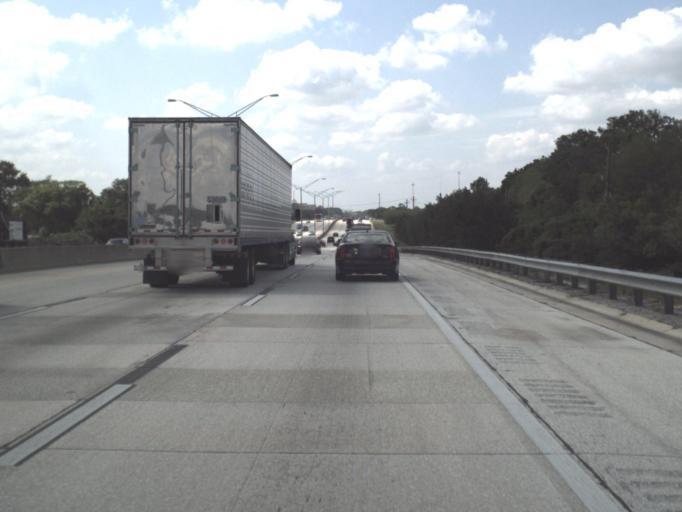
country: US
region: Florida
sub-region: Duval County
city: Jacksonville
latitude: 30.2651
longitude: -81.6089
